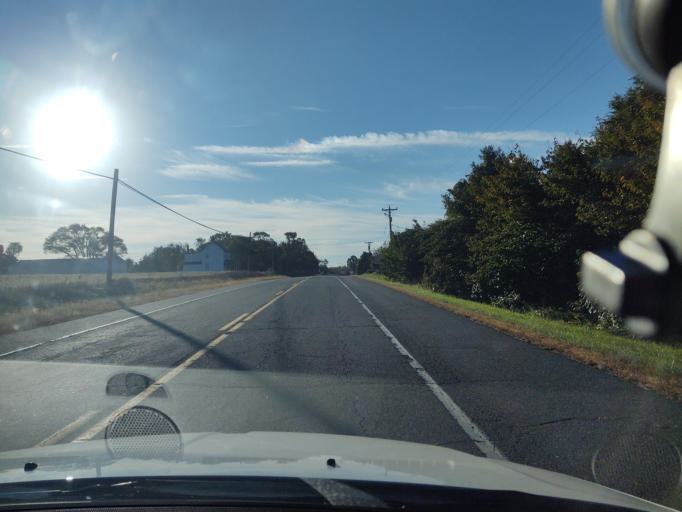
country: US
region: Maryland
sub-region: Queen Anne's County
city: Kingstown
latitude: 39.2355
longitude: -75.9166
